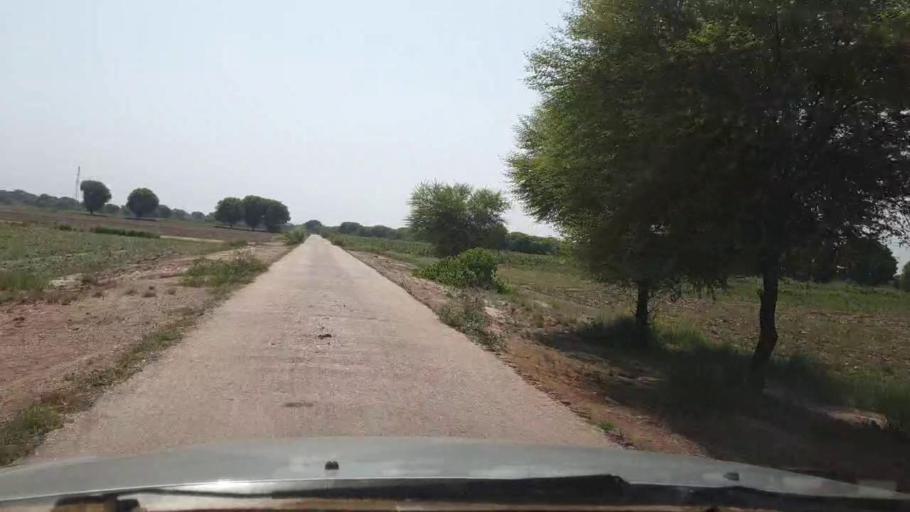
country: PK
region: Sindh
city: Chambar
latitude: 25.2257
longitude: 68.7777
